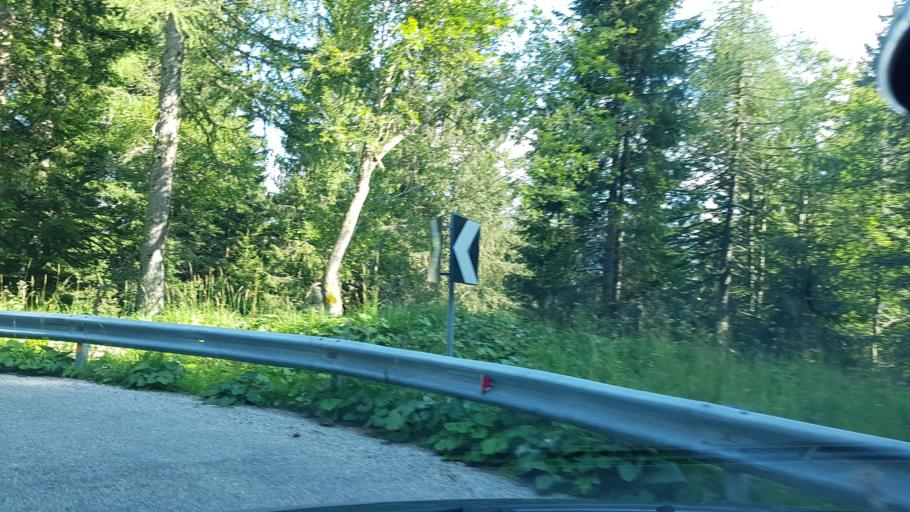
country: IT
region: Friuli Venezia Giulia
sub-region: Provincia di Udine
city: Sauris di Sotto
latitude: 46.4719
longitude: 12.6446
